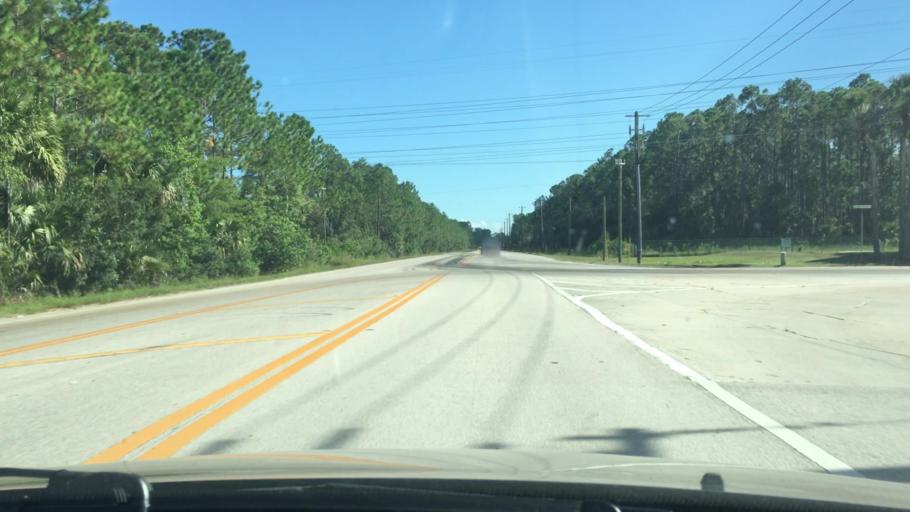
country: US
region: Florida
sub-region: Volusia County
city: South Daytona
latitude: 29.1292
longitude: -81.0741
